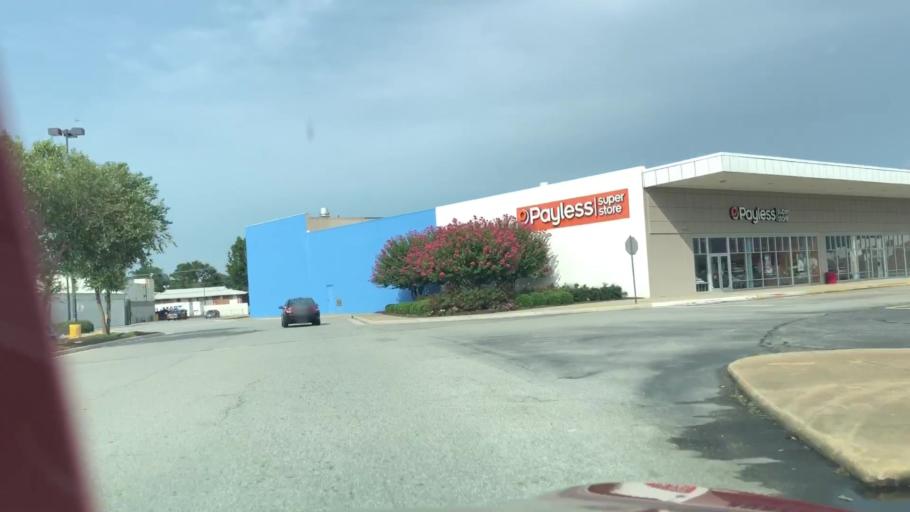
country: US
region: Virginia
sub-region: City of Norfolk
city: Norfolk
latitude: 36.8612
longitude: -76.2077
